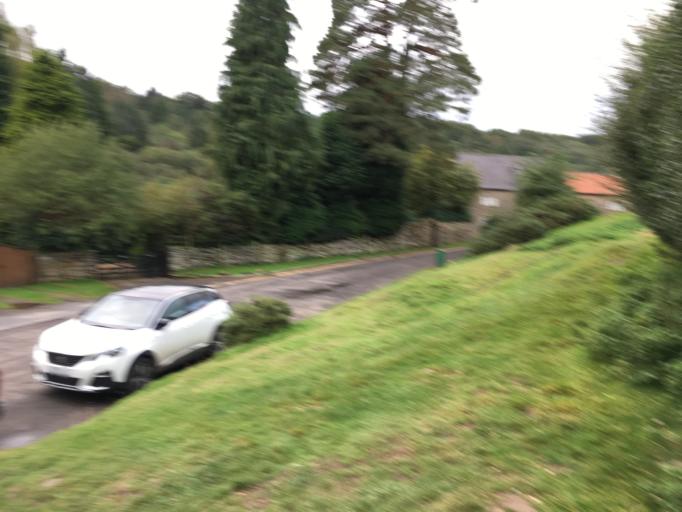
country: GB
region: England
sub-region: North Yorkshire
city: Sleights
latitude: 54.4092
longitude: -0.7360
